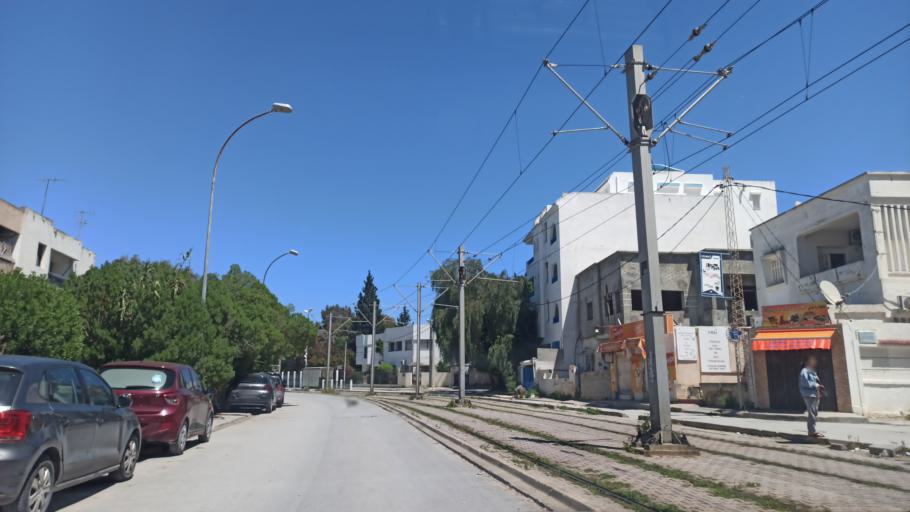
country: TN
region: Tunis
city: Tunis
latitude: 36.8226
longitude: 10.1849
